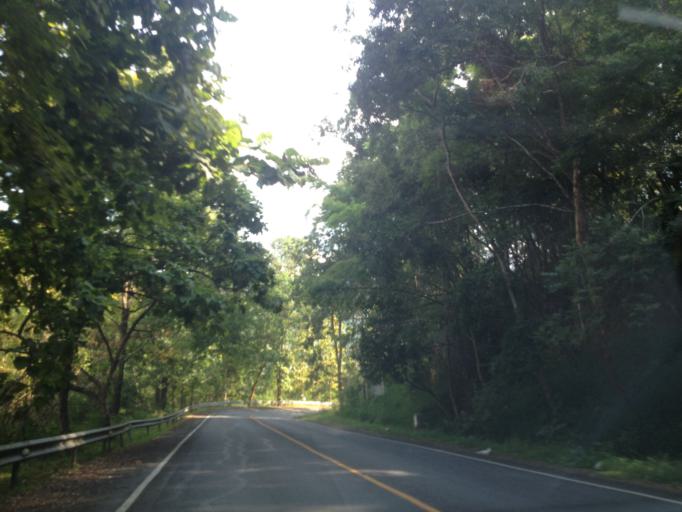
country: TH
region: Chiang Mai
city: Samoeng
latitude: 18.8191
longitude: 98.7889
